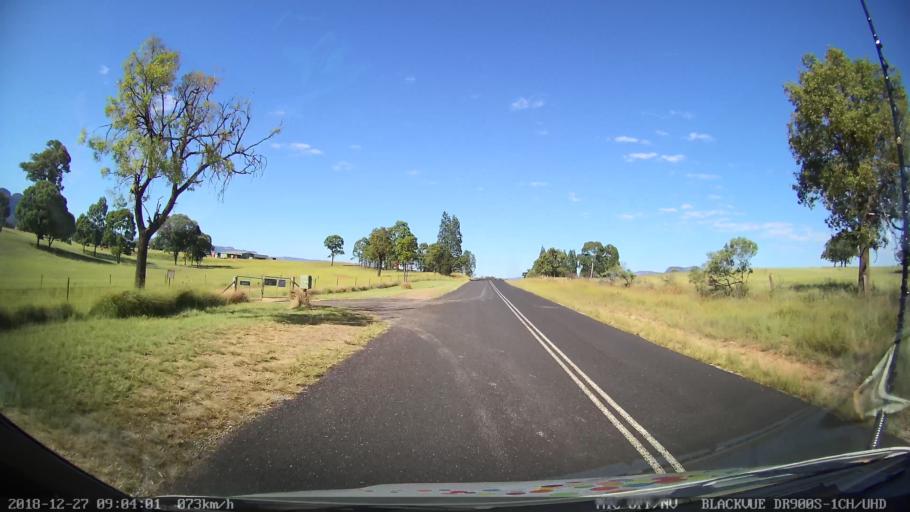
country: AU
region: New South Wales
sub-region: Lithgow
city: Portland
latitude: -33.1081
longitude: 150.1950
